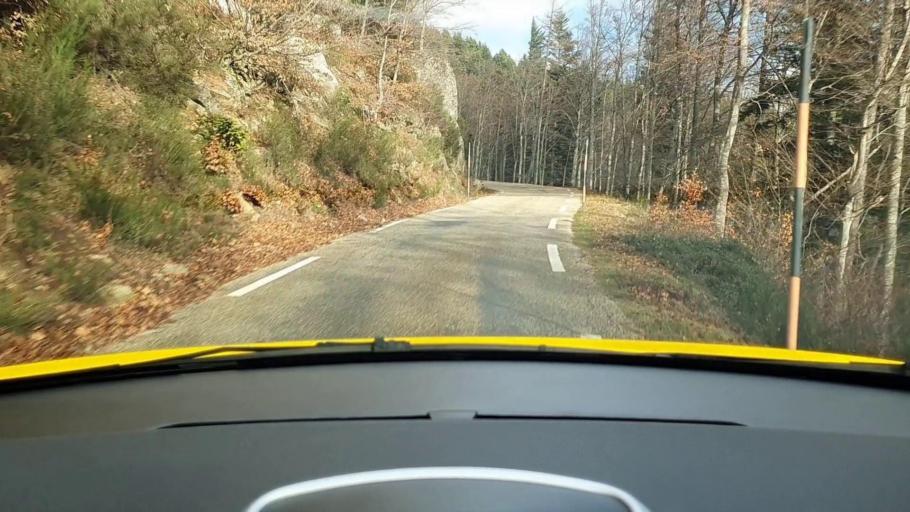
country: FR
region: Languedoc-Roussillon
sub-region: Departement du Gard
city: Branoux-les-Taillades
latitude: 44.3664
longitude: 3.9203
